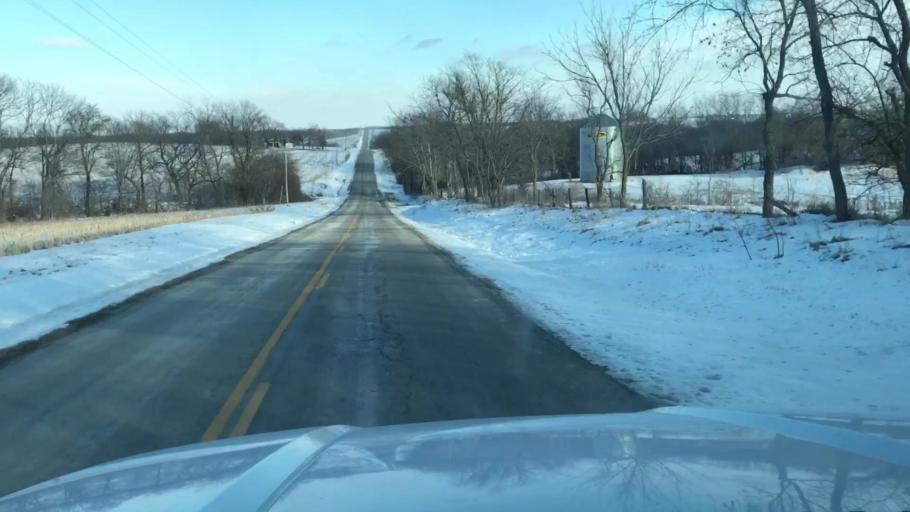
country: US
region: Missouri
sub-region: Holt County
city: Oregon
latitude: 40.1008
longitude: -95.0126
